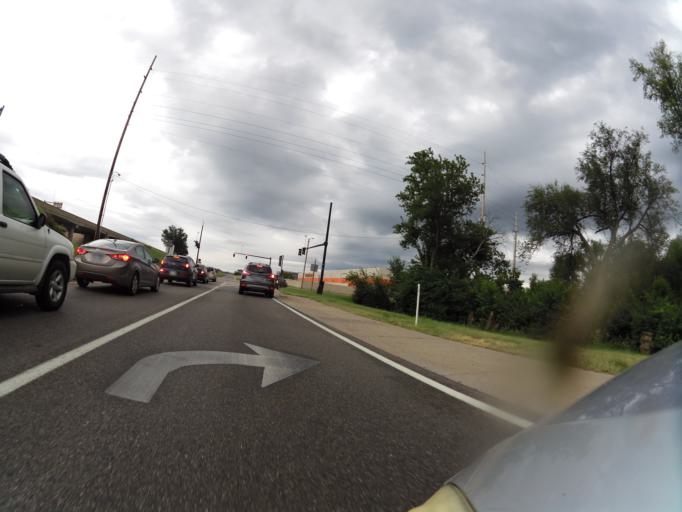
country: US
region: Kansas
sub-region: Sedgwick County
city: Bellaire
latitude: 37.7450
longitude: -97.2631
